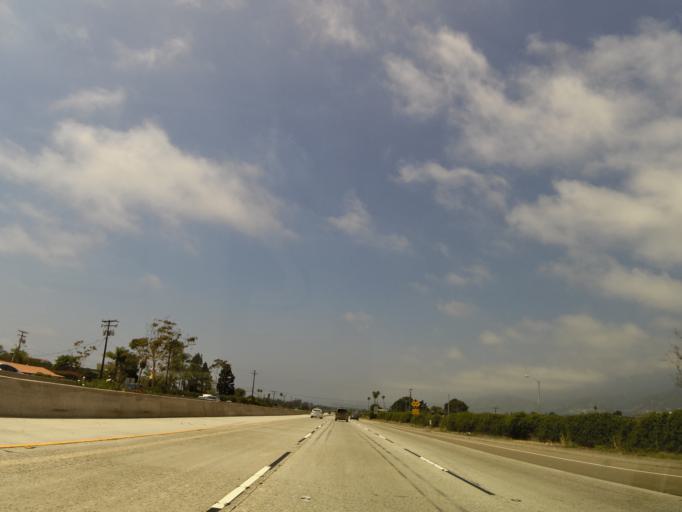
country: US
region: California
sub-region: Santa Barbara County
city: Carpinteria
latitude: 34.3854
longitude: -119.4886
